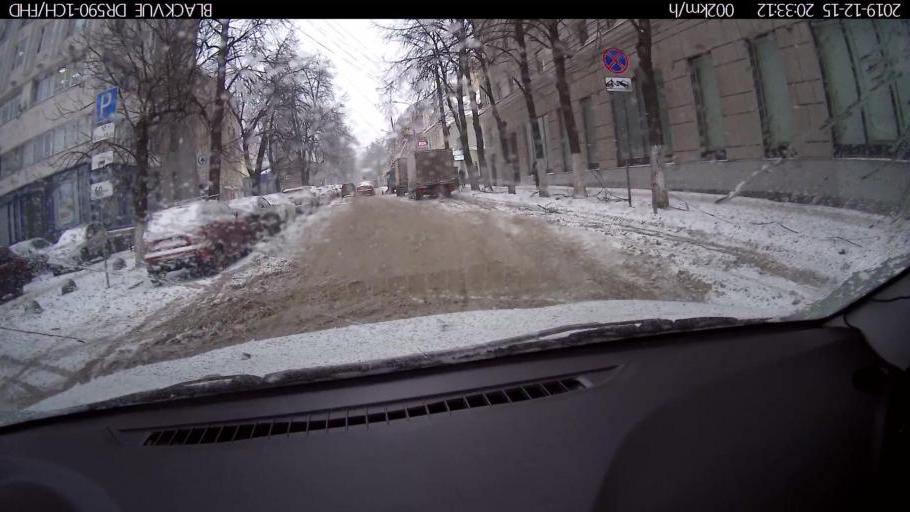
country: RU
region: Nizjnij Novgorod
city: Nizhniy Novgorod
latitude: 56.3131
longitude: 43.9916
